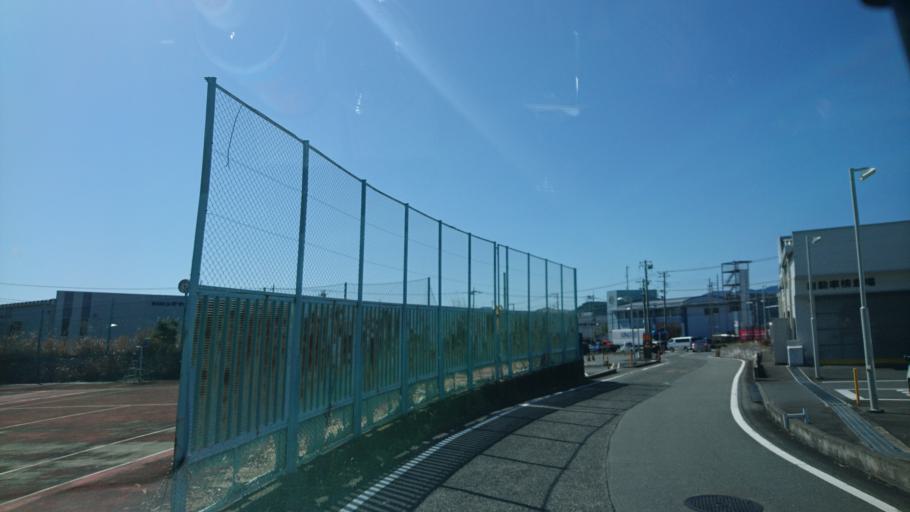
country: JP
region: Shizuoka
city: Fujinomiya
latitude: 35.2458
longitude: 138.6111
